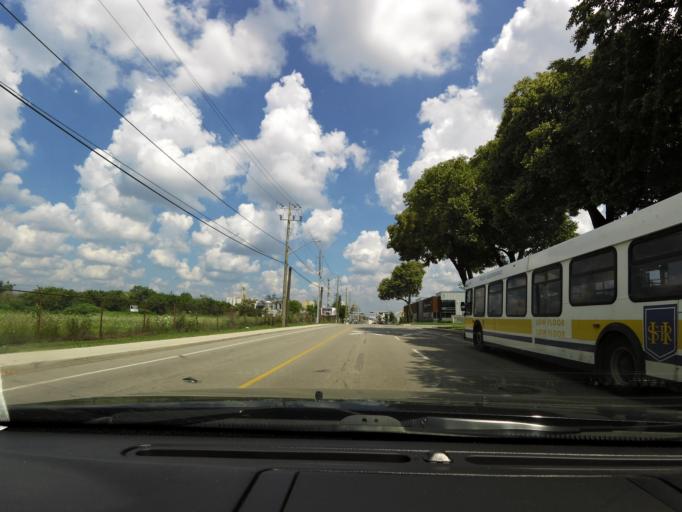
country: CA
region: Ontario
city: Hamilton
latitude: 43.2667
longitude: -79.8508
